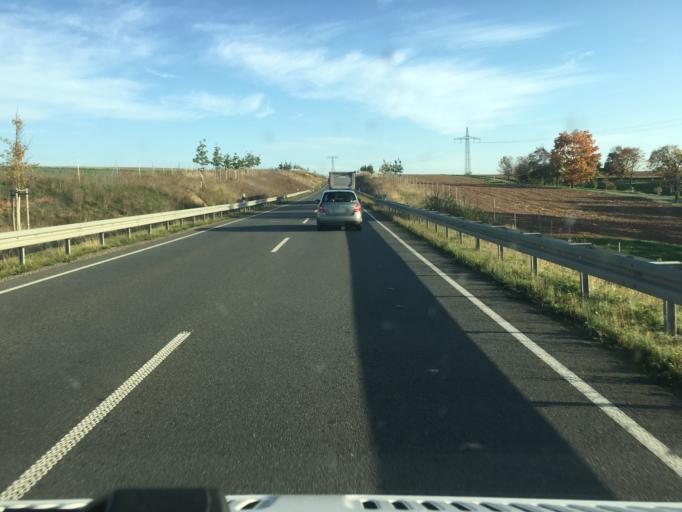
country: DE
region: Saxony
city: Neukirchen
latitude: 50.7903
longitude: 12.3649
